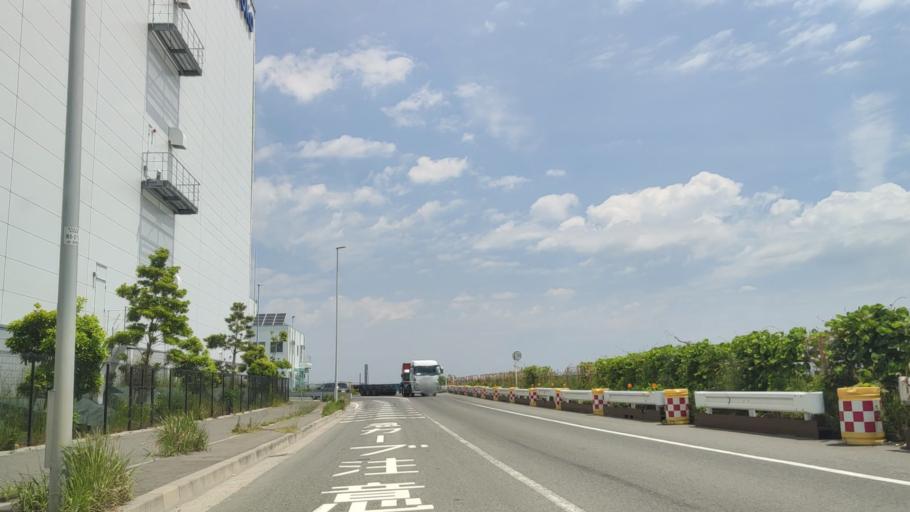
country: JP
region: Kanagawa
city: Yokohama
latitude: 35.4061
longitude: 139.6869
